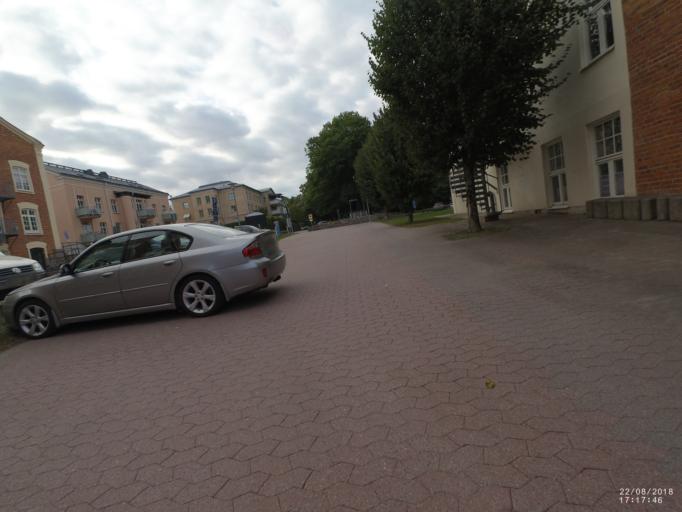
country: SE
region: Soedermanland
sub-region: Nykopings Kommun
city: Nykoping
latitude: 58.7561
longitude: 17.0076
